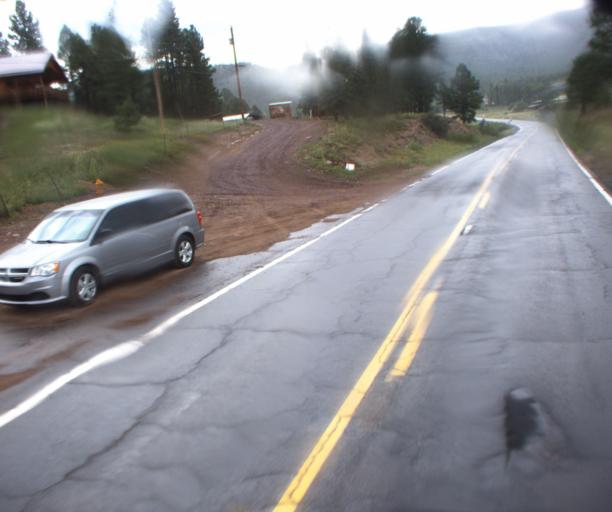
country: US
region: Arizona
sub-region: Apache County
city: Eagar
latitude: 33.8432
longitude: -109.1483
